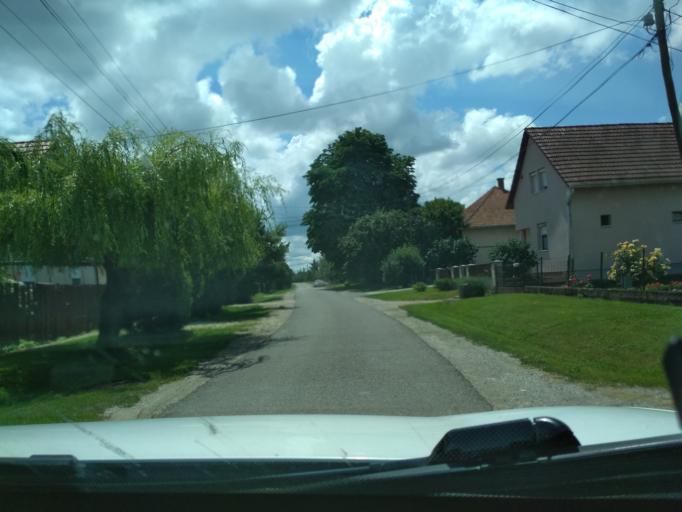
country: HU
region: Jasz-Nagykun-Szolnok
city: Tiszafured
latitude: 47.6097
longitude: 20.7776
